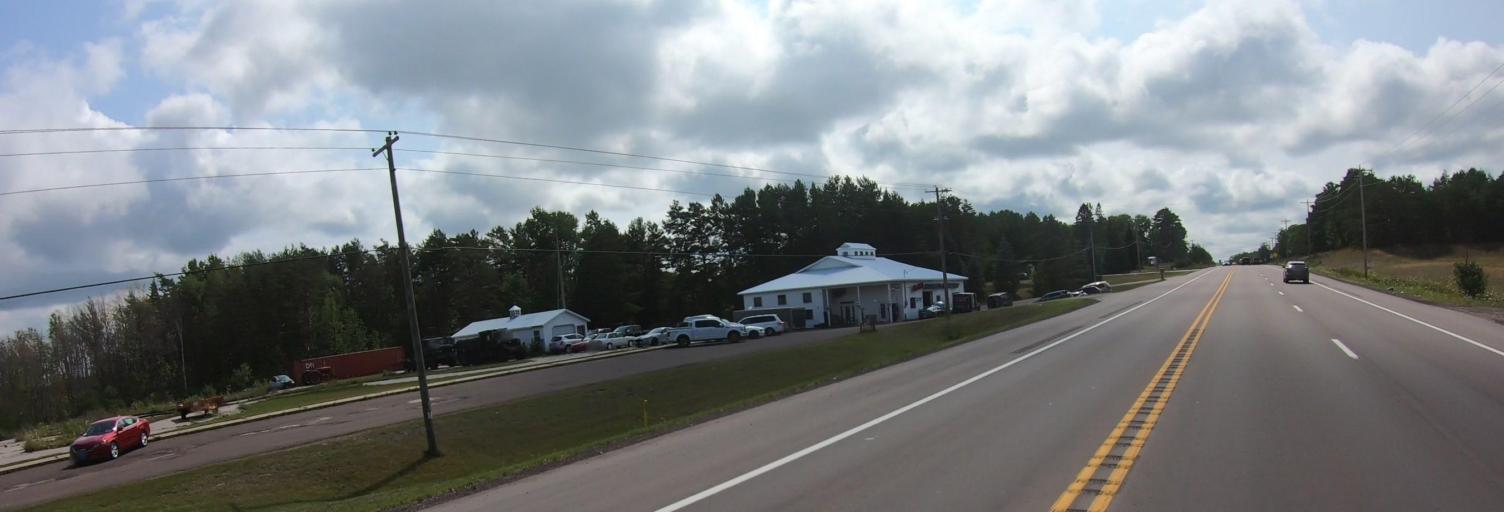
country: US
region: Michigan
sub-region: Houghton County
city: Hancock
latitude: 47.1008
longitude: -88.6068
